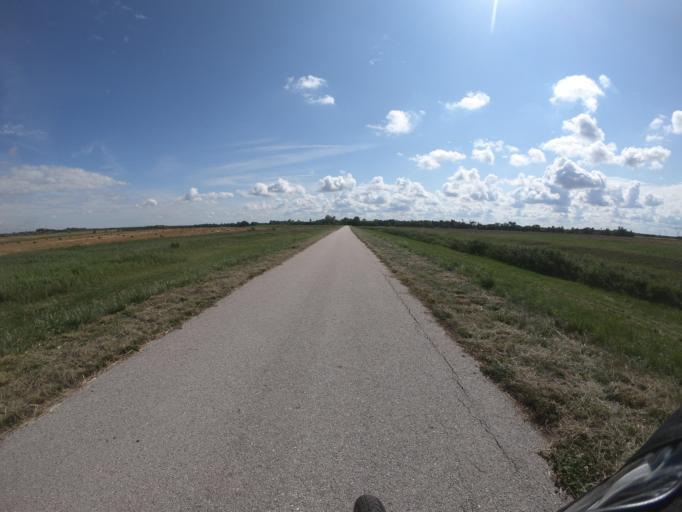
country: HU
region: Borsod-Abauj-Zemplen
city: Szentistvan
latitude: 47.7146
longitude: 20.6871
